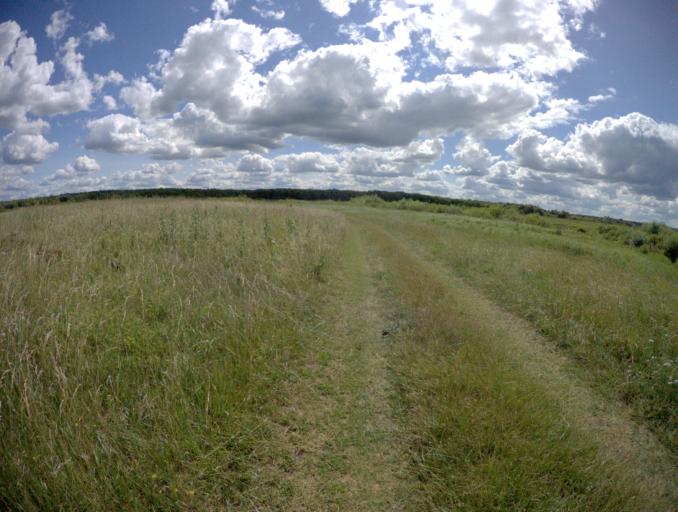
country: RU
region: Vladimir
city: Orgtrud
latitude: 56.3007
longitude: 40.6258
